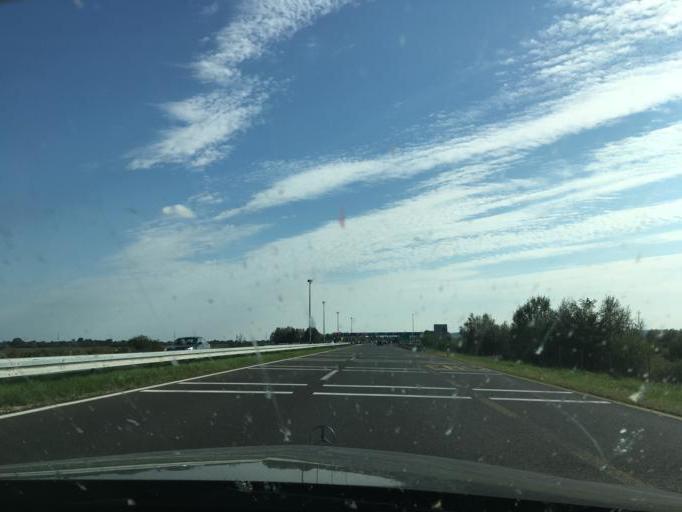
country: HR
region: Zagrebacka
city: Brckovljani
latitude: 45.9242
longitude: 16.2725
